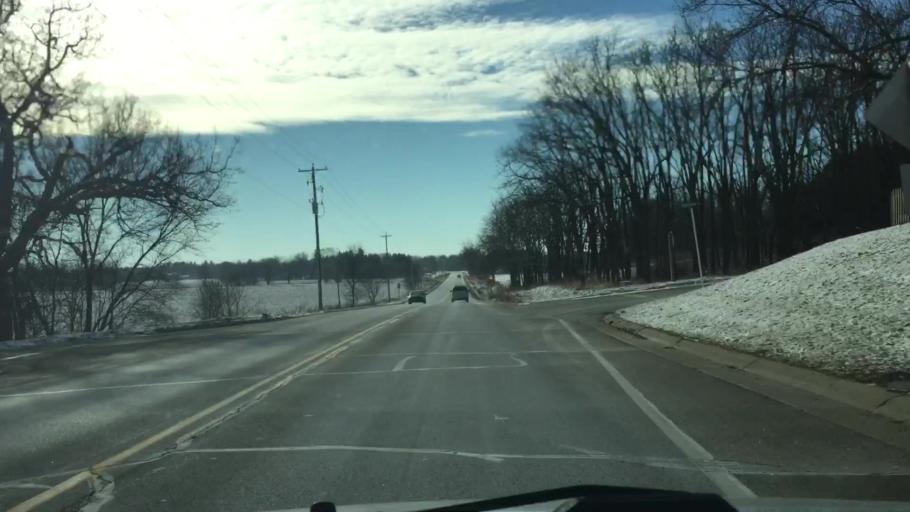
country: US
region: Wisconsin
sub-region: Jefferson County
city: Palmyra
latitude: 42.7965
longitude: -88.5630
